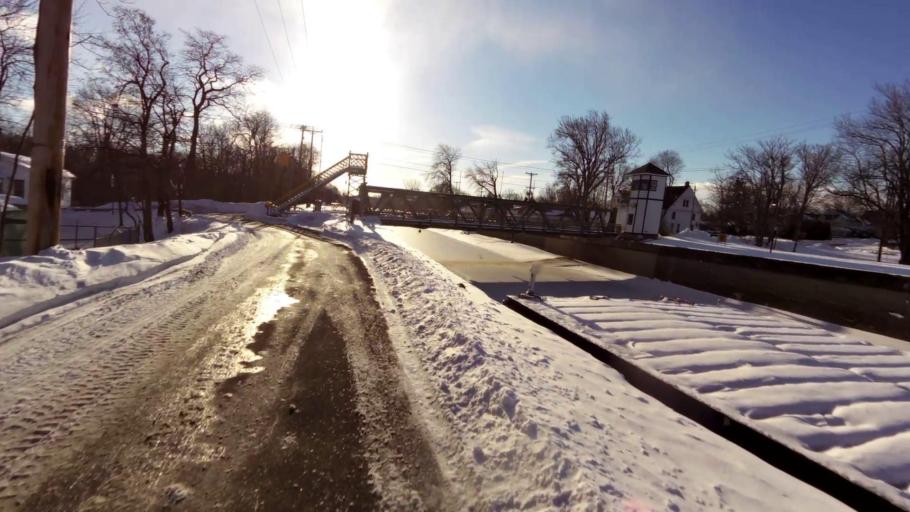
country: US
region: New York
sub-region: Orleans County
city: Albion
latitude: 43.2488
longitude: -78.1909
